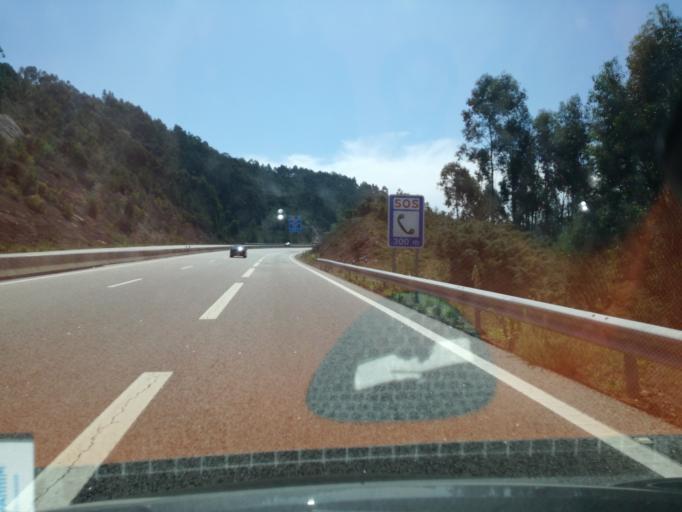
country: PT
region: Viana do Castelo
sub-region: Vila Nova de Cerveira
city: Vila Nova de Cerveira
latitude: 41.8678
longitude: -8.7821
